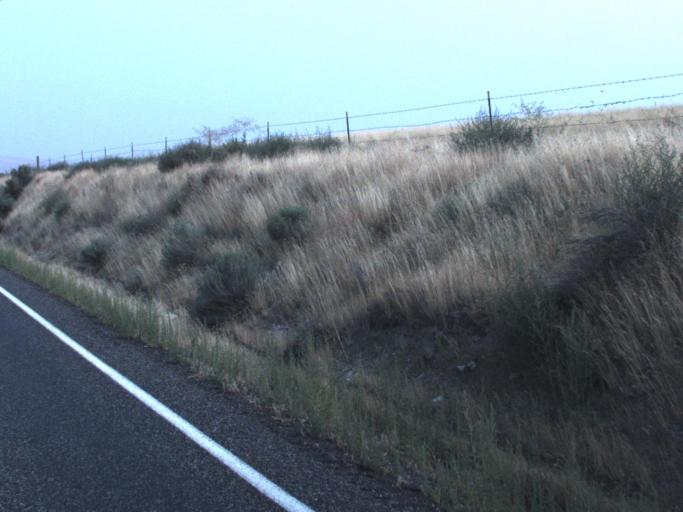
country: US
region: Washington
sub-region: Grant County
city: Desert Aire
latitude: 46.4966
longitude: -119.9025
